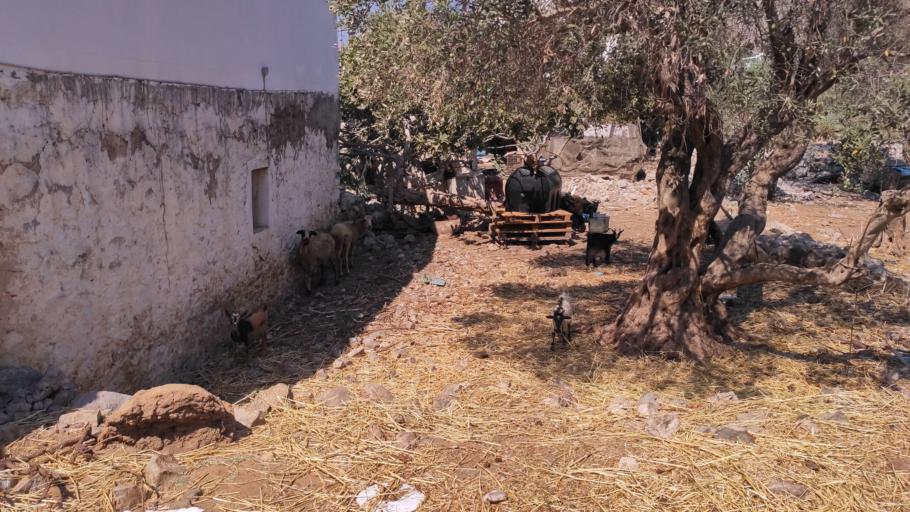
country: GR
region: South Aegean
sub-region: Nomos Dodekanisou
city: Pylion
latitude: 36.9324
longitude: 27.1352
